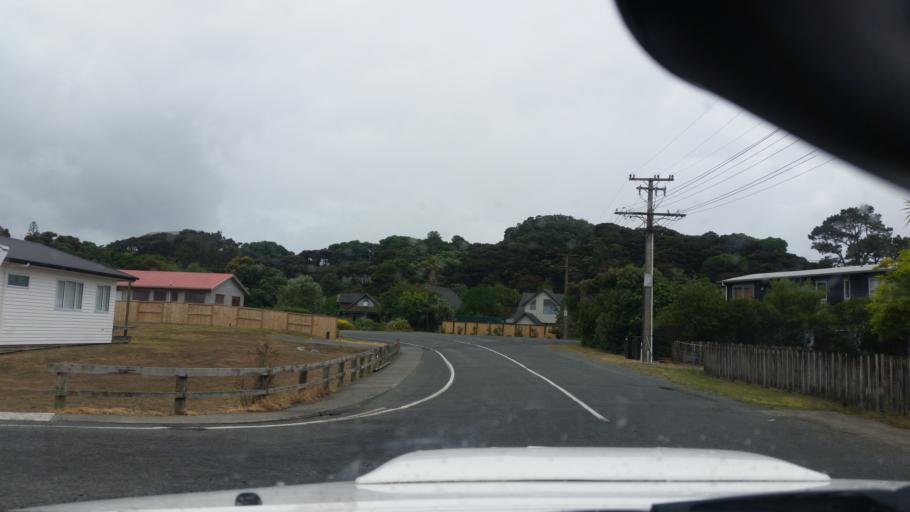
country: NZ
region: Auckland
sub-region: Auckland
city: Wellsford
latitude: -36.1032
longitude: 174.5909
